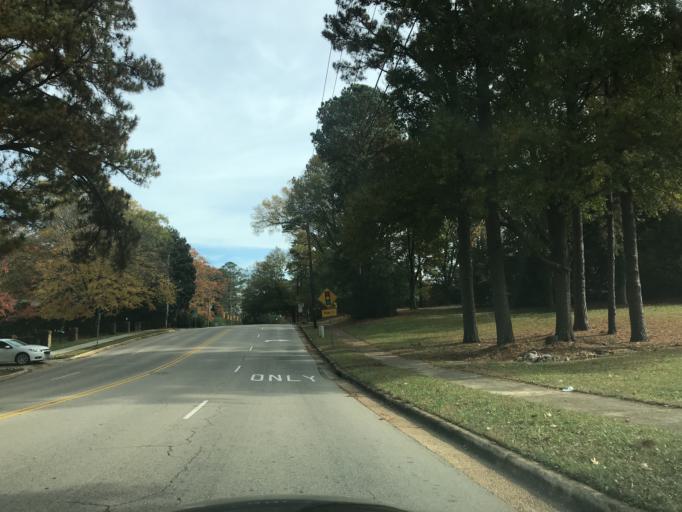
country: US
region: North Carolina
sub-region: Wake County
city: West Raleigh
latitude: 35.8145
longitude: -78.6792
